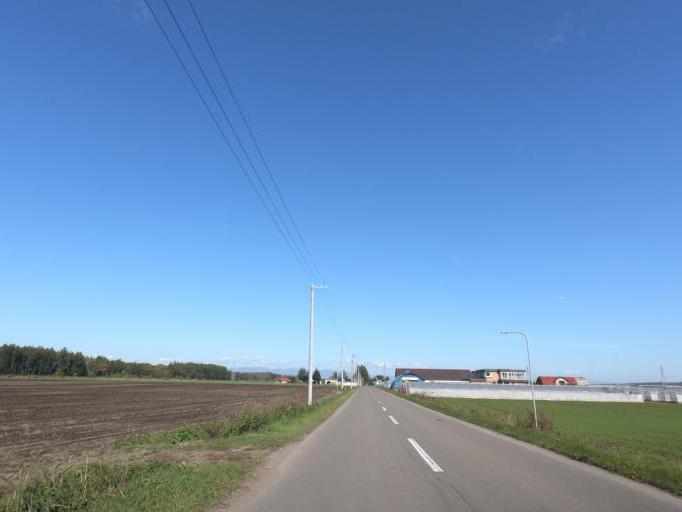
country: JP
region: Hokkaido
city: Obihiro
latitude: 42.9547
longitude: 143.2351
